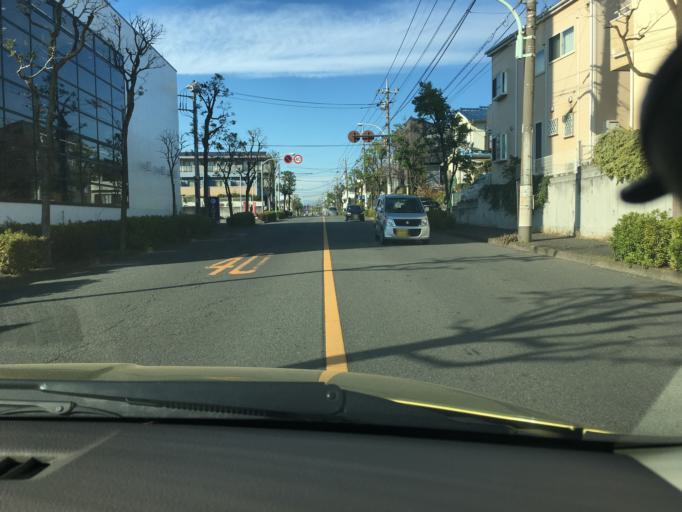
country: JP
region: Tokyo
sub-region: Machida-shi
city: Machida
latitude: 35.5652
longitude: 139.4197
